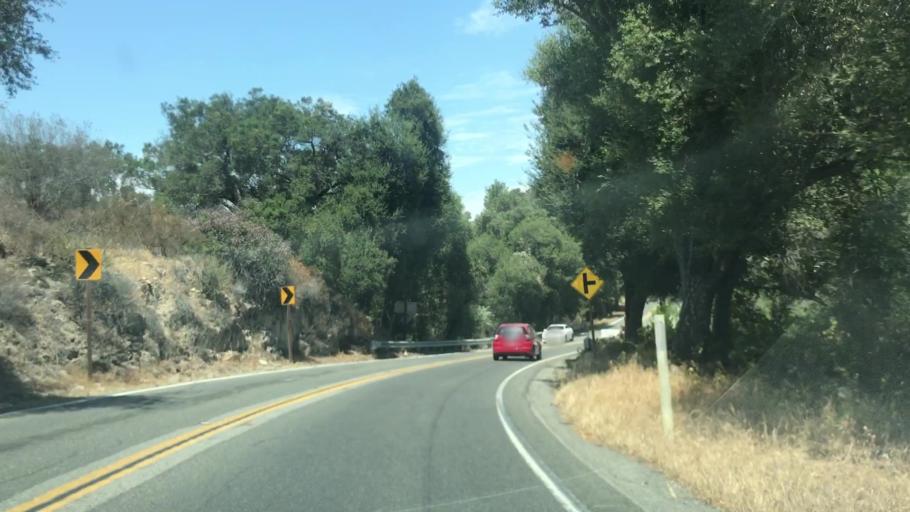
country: US
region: California
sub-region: Riverside County
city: Lakeland Village
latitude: 33.6158
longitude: -117.4263
